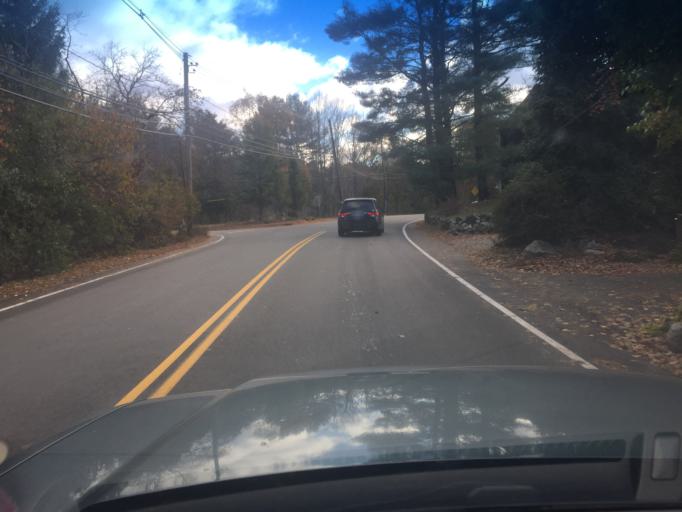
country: US
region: Massachusetts
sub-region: Norfolk County
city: Medfield
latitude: 42.1971
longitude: -71.3133
